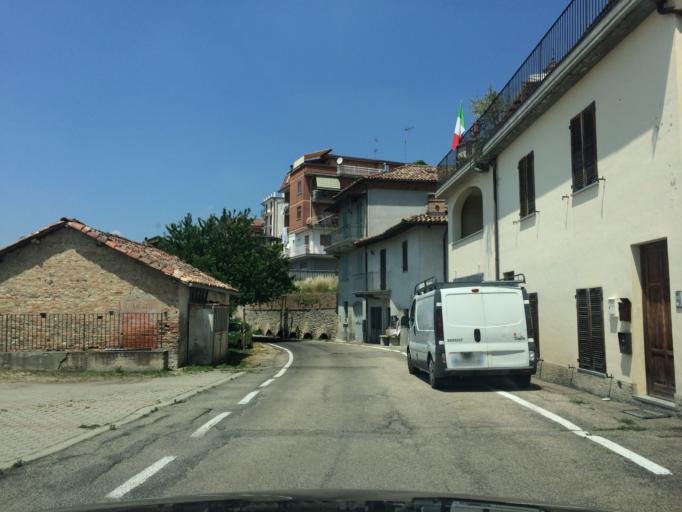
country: IT
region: Piedmont
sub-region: Provincia di Asti
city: Calosso
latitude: 44.7387
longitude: 8.2285
